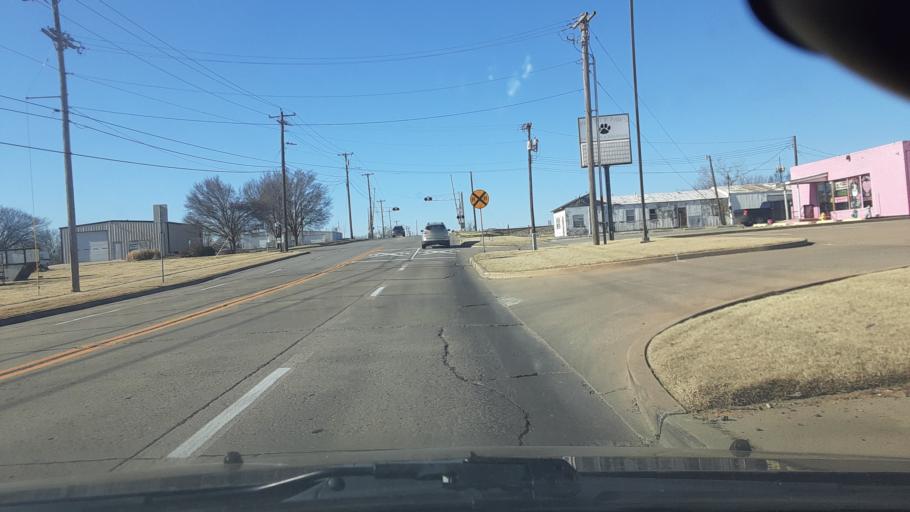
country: US
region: Oklahoma
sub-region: Kay County
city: Ponca City
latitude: 36.7242
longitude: -97.0803
